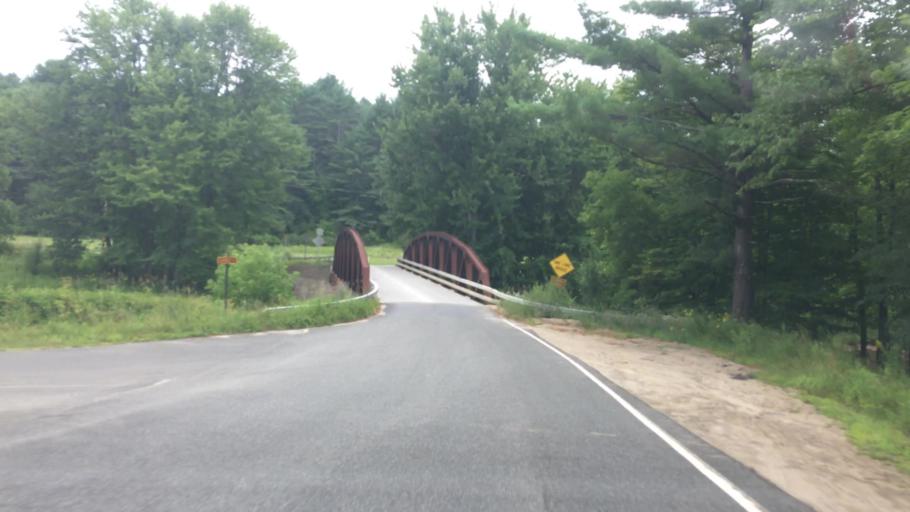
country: US
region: New York
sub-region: Essex County
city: Elizabethtown
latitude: 44.4127
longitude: -73.6805
